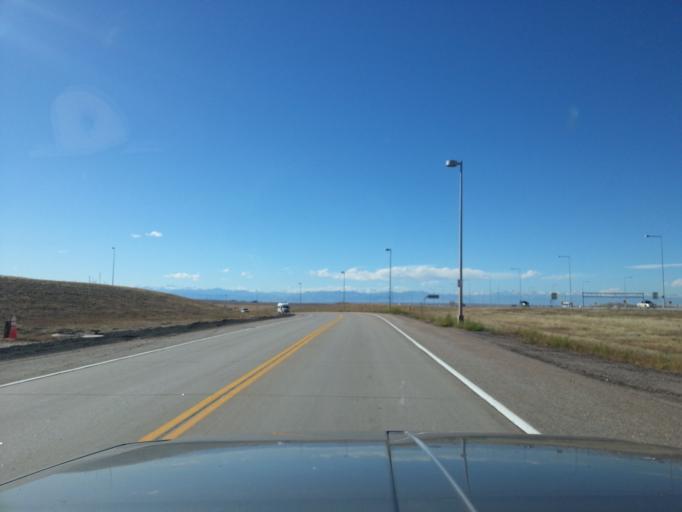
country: US
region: Colorado
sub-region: Adams County
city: Aurora
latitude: 39.8331
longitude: -104.7093
